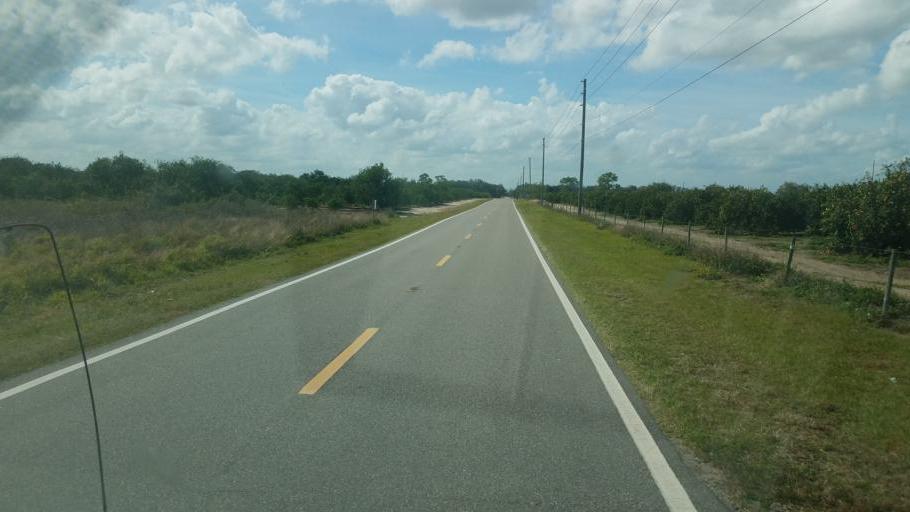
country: US
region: Florida
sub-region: Polk County
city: Lake Wales
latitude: 27.9252
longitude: -81.5022
